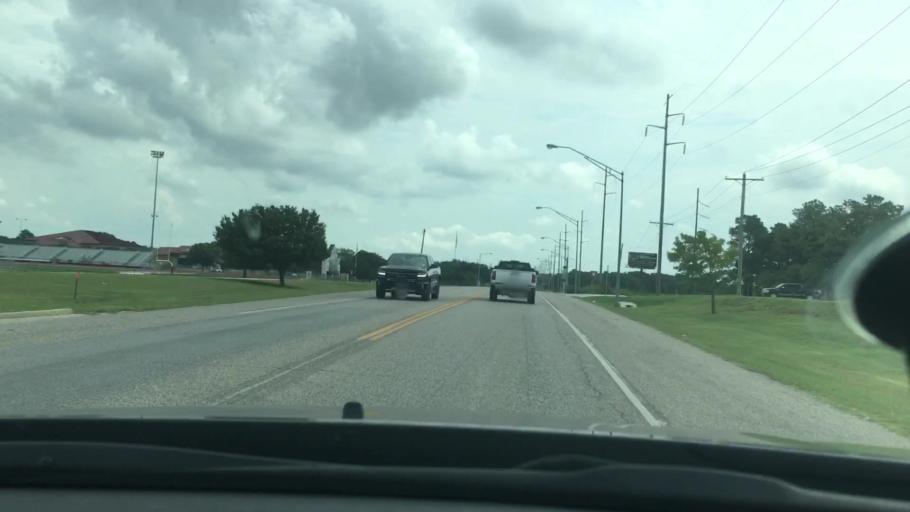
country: US
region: Oklahoma
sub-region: Carter County
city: Ardmore
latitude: 34.2029
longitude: -97.1388
